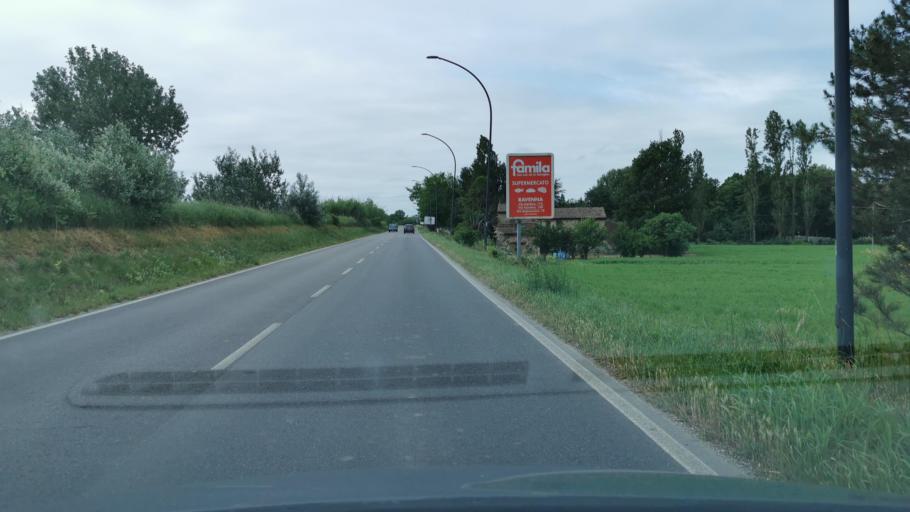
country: IT
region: Emilia-Romagna
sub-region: Provincia di Ravenna
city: Madonna Dell'Albero
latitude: 44.3930
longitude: 12.1971
